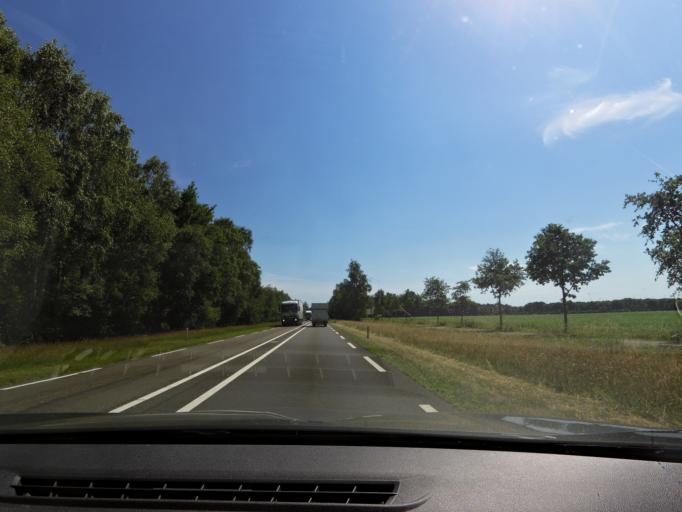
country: NL
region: Gelderland
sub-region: Oost Gelre
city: Lichtenvoorde
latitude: 52.0250
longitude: 6.6152
